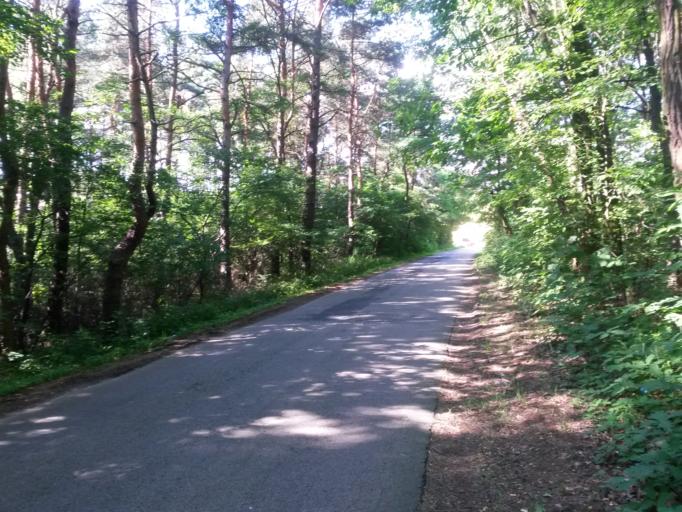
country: PL
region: Silesian Voivodeship
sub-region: Powiat bedzinski
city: Siewierz
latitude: 50.4236
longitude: 19.2268
